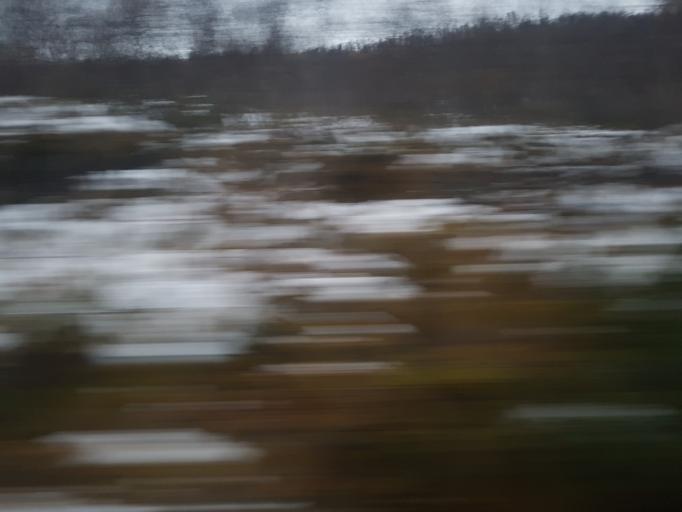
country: NO
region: Sor-Trondelag
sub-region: Oppdal
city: Oppdal
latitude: 62.3297
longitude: 9.6201
